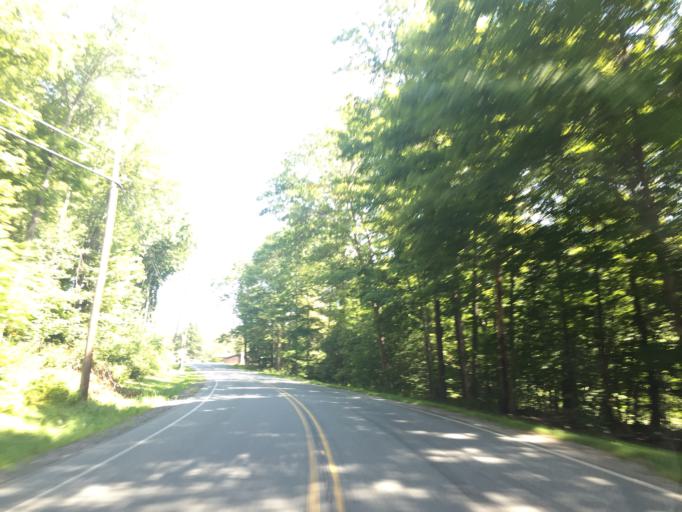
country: US
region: New York
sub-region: Sullivan County
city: Livingston Manor
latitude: 41.8278
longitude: -74.9506
